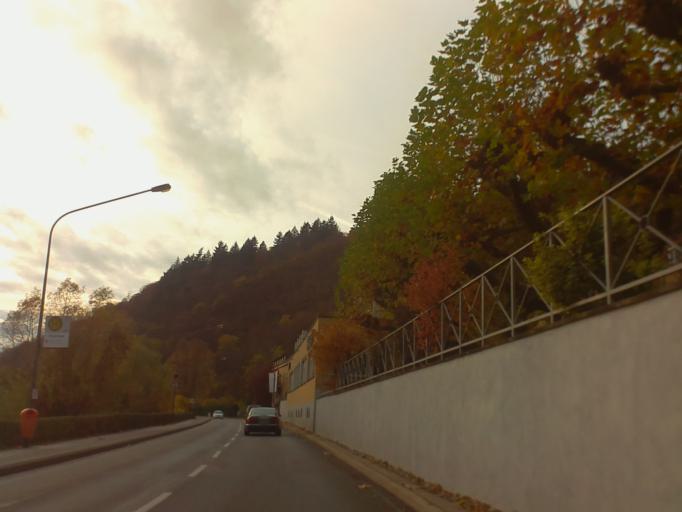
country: DE
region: Baden-Wuerttemberg
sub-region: Karlsruhe Region
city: Heidelberg
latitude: 49.4202
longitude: 8.7308
